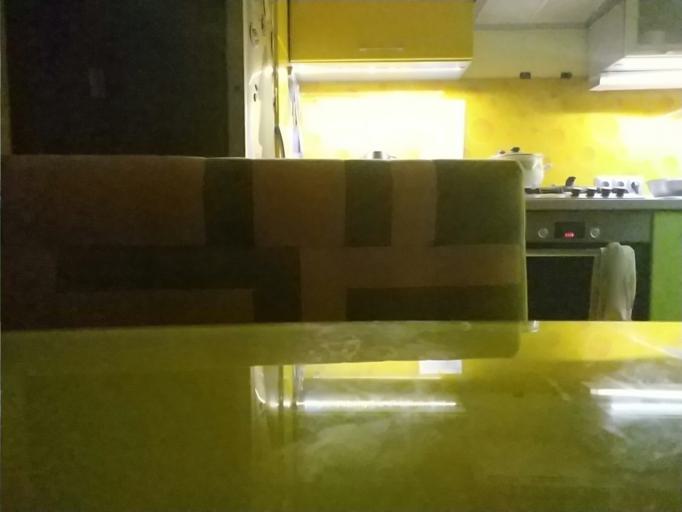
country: RU
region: Republic of Karelia
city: Pyaozerskiy
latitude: 65.8983
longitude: 30.4281
